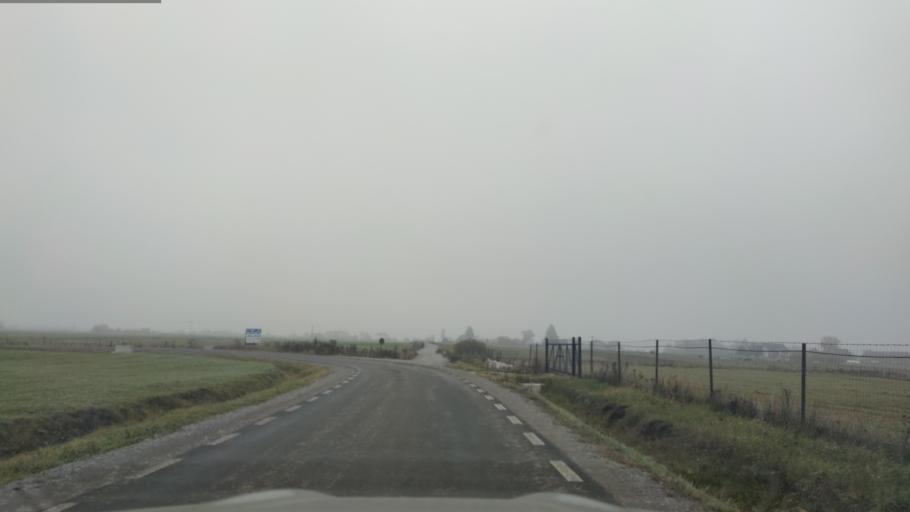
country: RO
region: Harghita
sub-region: Comuna Remetea
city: Remetea
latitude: 46.8047
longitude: 25.4318
